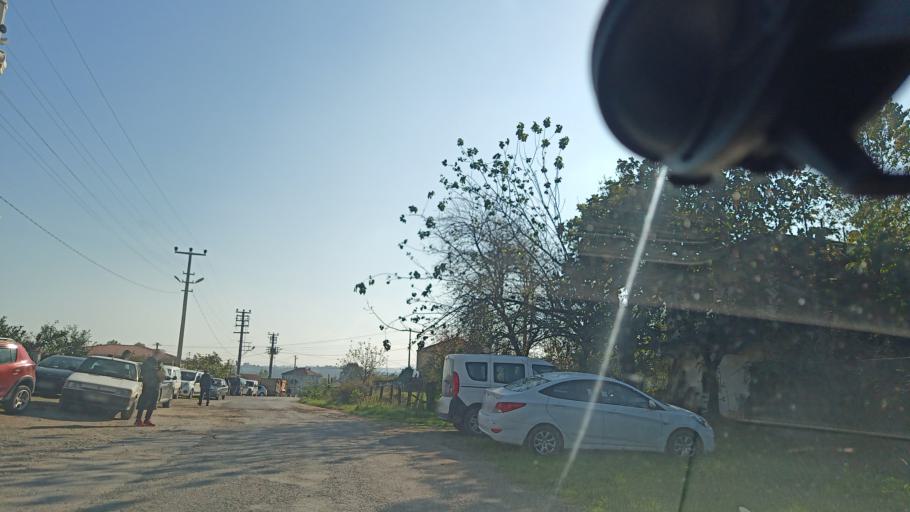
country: TR
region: Sakarya
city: Karasu
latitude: 41.0712
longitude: 30.8022
